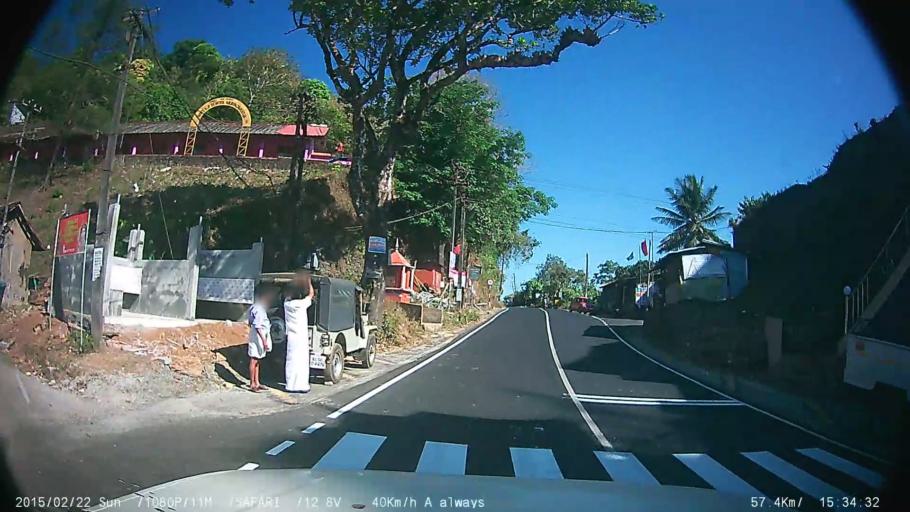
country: IN
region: Kerala
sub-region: Kottayam
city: Erattupetta
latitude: 9.5545
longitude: 76.9719
